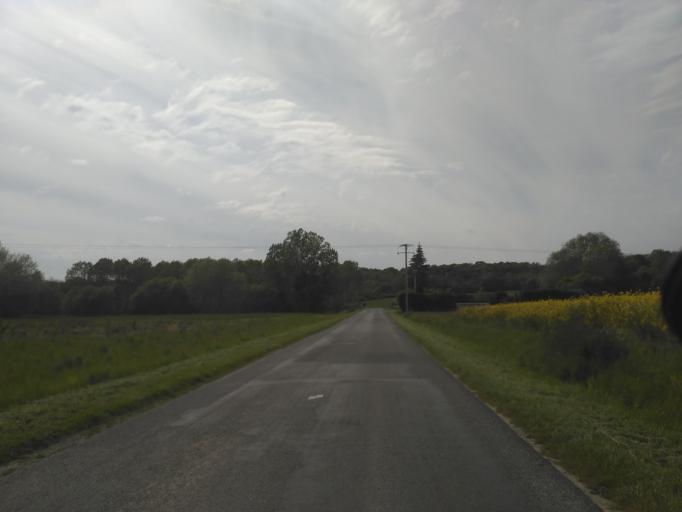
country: FR
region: Ile-de-France
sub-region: Departement de Seine-et-Marne
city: Chaumes-en-Brie
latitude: 48.6662
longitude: 2.8240
